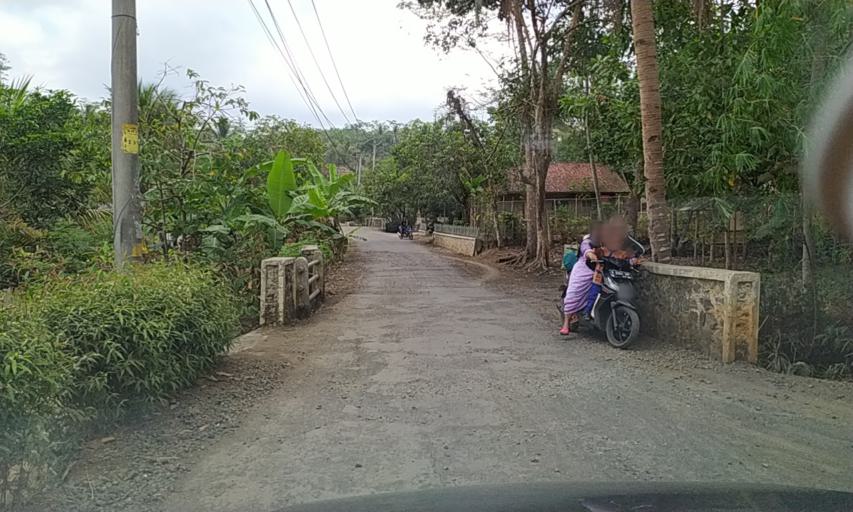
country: ID
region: Central Java
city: Ciwalen
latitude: -7.2874
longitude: 108.6193
